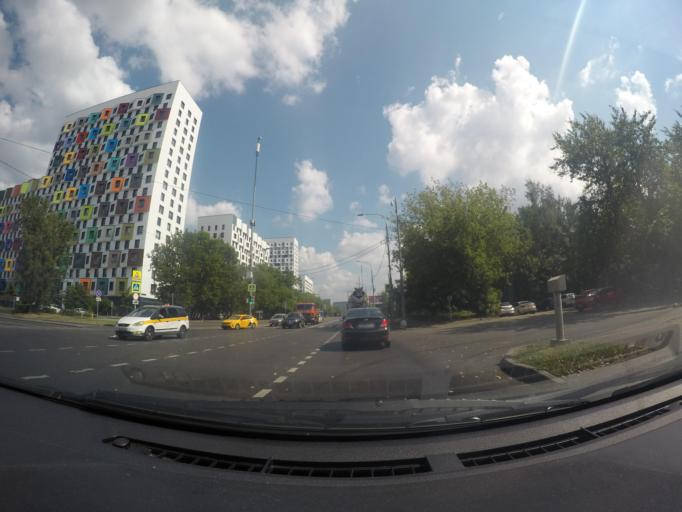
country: RU
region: Moscow
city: Kozeyevo
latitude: 55.8502
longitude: 37.6157
